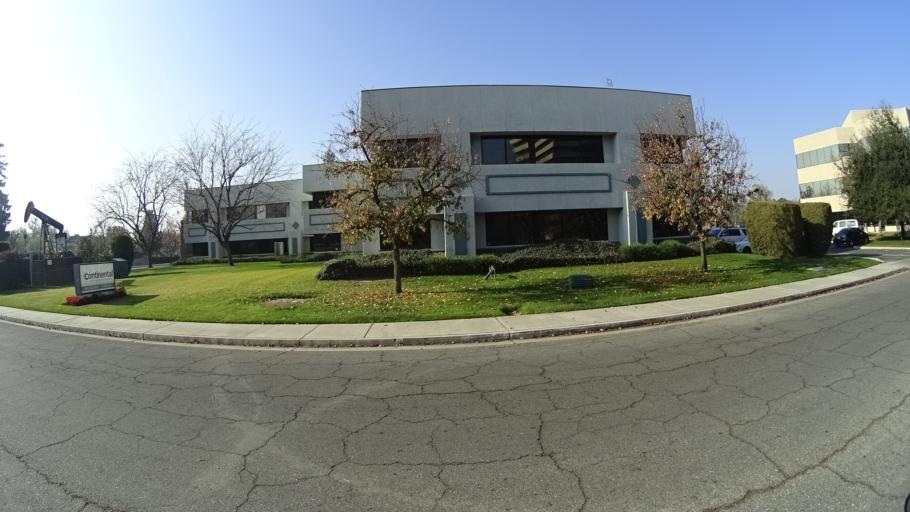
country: US
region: California
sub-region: Kern County
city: Bakersfield
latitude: 35.3626
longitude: -119.0619
